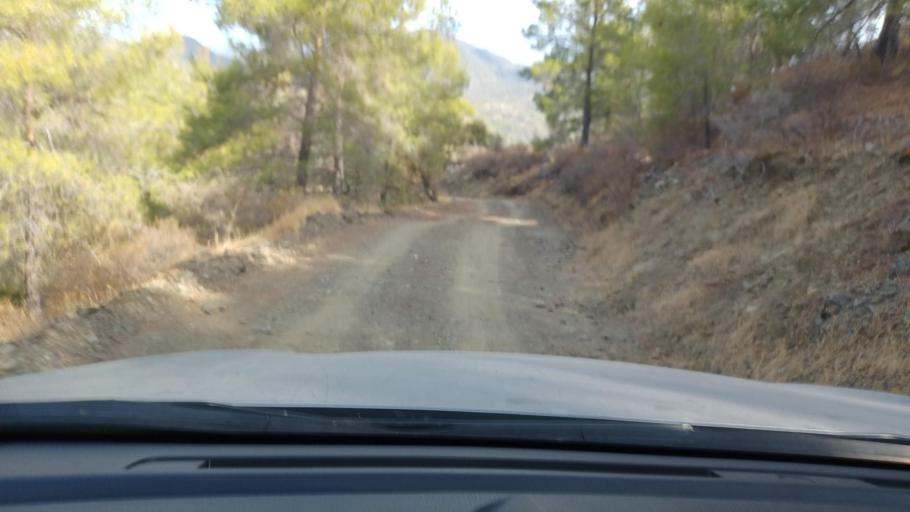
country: CY
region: Pafos
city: Polis
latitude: 35.0173
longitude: 32.5306
